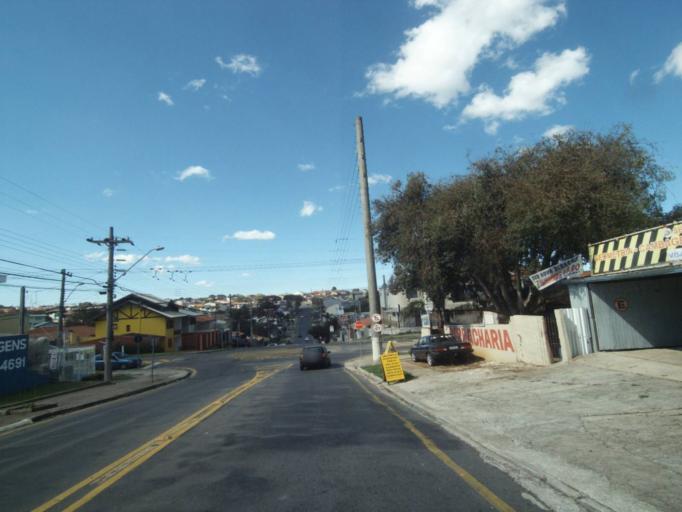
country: BR
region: Parana
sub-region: Curitiba
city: Curitiba
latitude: -25.3798
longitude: -49.2555
